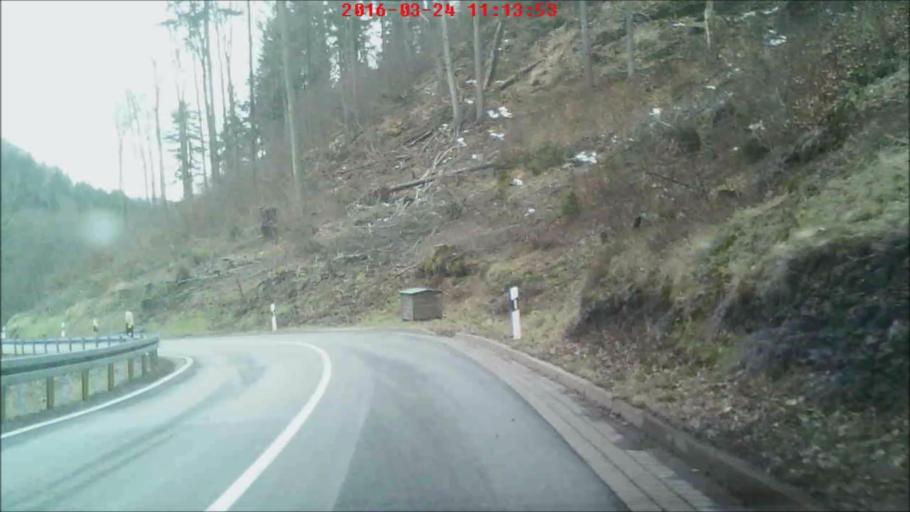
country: DE
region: Thuringia
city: Masserberg
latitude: 50.5151
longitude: 10.9565
